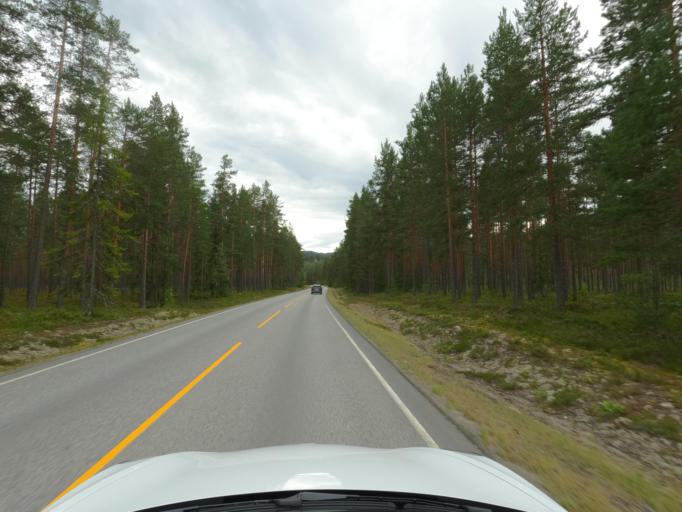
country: NO
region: Telemark
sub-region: Hjartdal
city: Sauland
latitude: 59.7157
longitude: 9.0170
